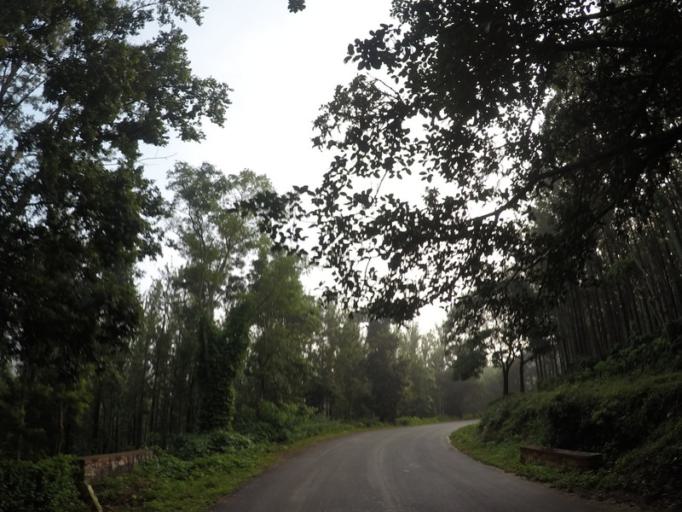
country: IN
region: Karnataka
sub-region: Chikmagalur
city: Chikmagalur
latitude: 13.3845
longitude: 75.7575
